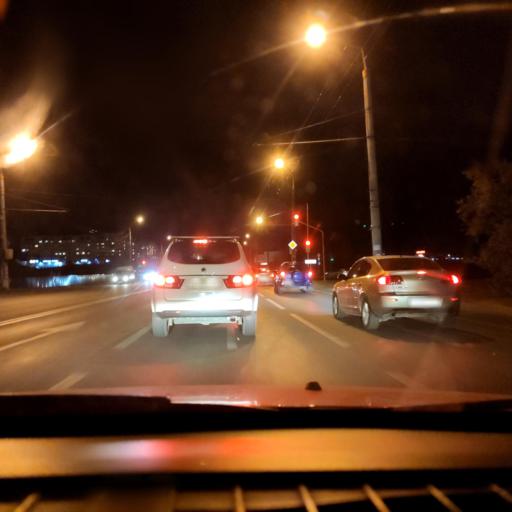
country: RU
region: Samara
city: Tol'yatti
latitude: 53.5494
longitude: 49.3333
